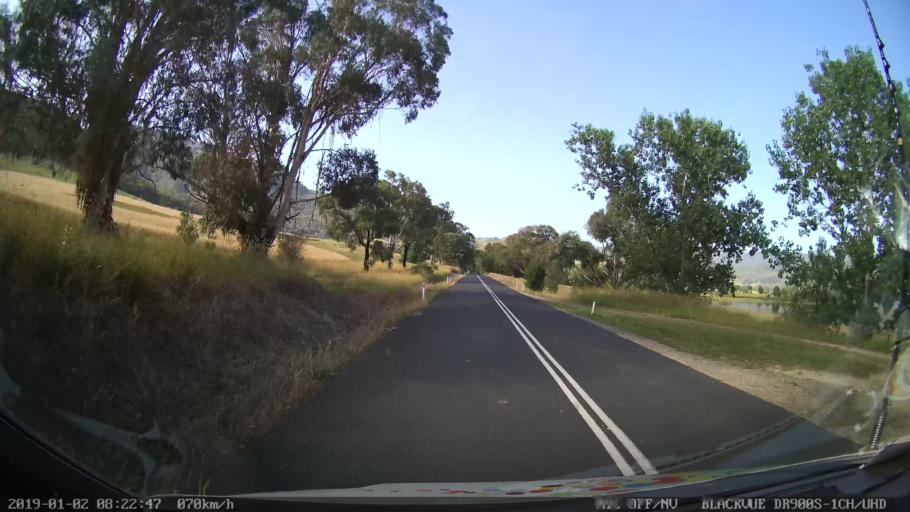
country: AU
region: New South Wales
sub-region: Tumut Shire
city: Tumut
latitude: -35.5735
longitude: 148.3119
